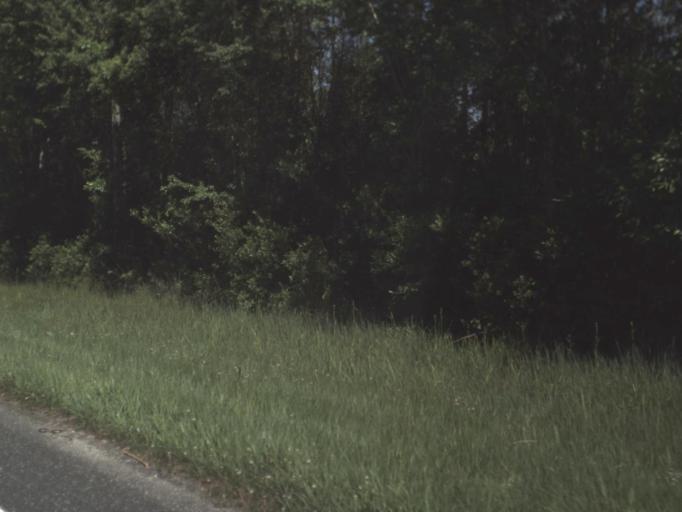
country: US
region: Florida
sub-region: Columbia County
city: Watertown
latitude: 30.2038
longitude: -82.4352
